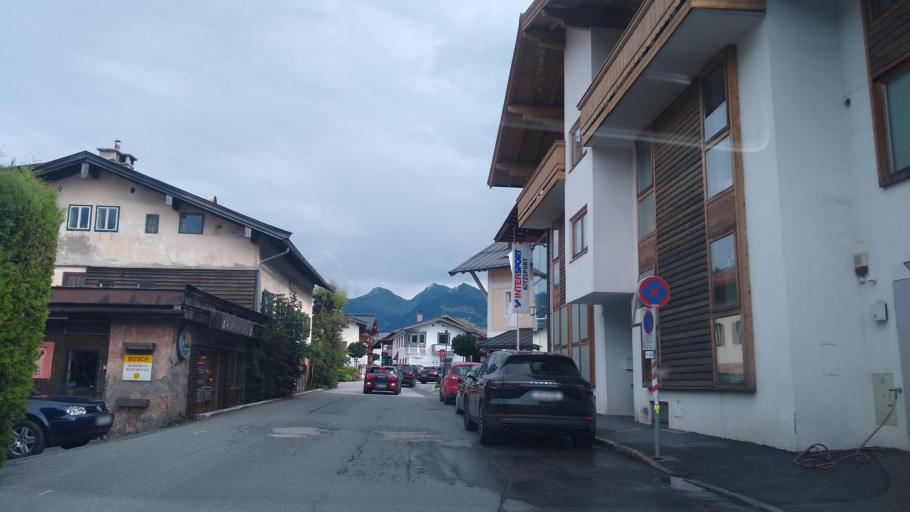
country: AT
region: Tyrol
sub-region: Politischer Bezirk Kitzbuhel
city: Kitzbuhel
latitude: 47.4447
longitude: 12.3955
